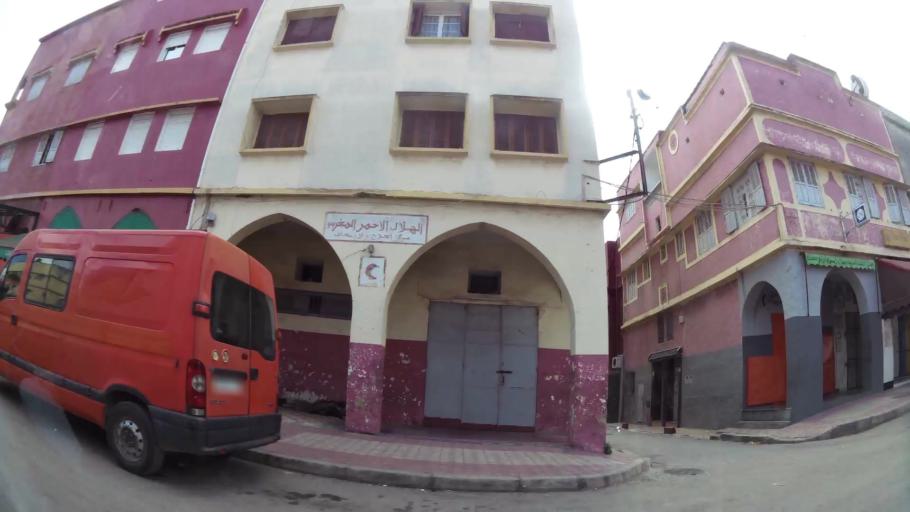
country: MA
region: Gharb-Chrarda-Beni Hssen
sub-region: Kenitra Province
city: Kenitra
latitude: 34.2653
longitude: -6.5615
